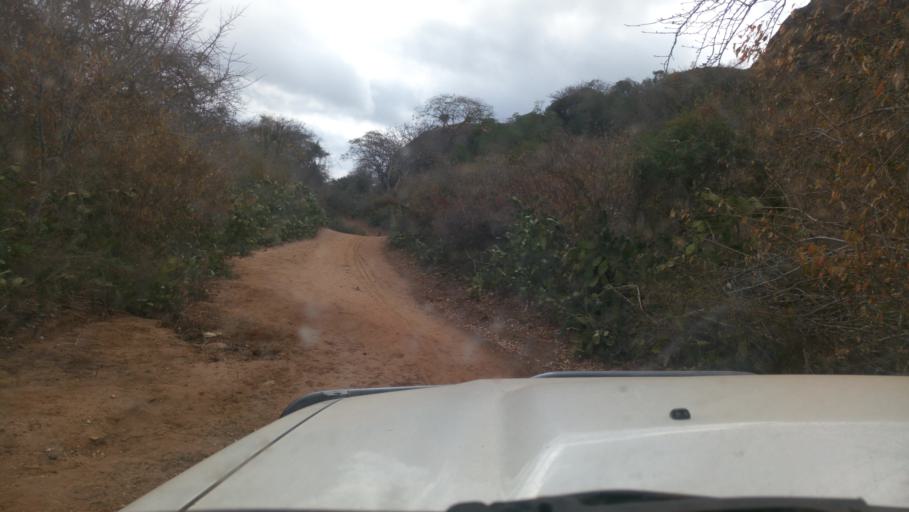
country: KE
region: Kitui
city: Kitui
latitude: -1.8551
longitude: 38.2503
